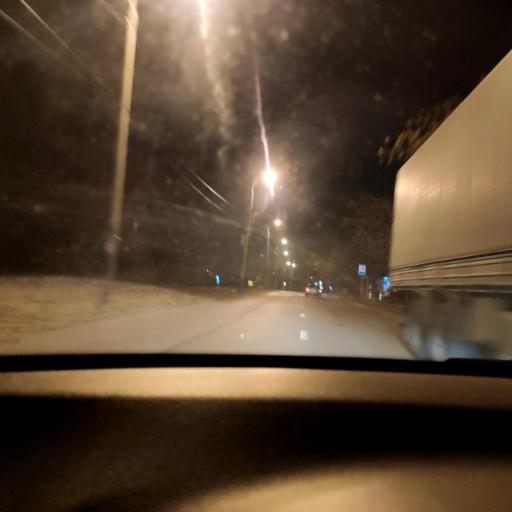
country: RU
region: Samara
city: Samara
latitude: 53.2470
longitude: 50.2114
